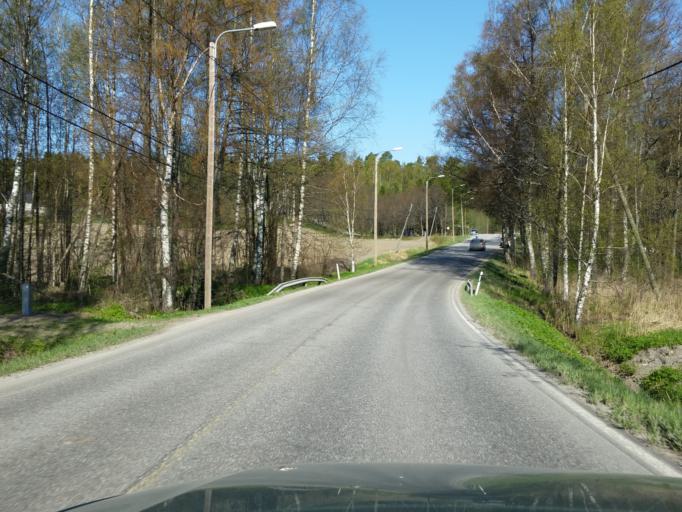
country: FI
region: Uusimaa
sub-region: Helsinki
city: Kirkkonummi
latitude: 60.1545
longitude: 24.4018
